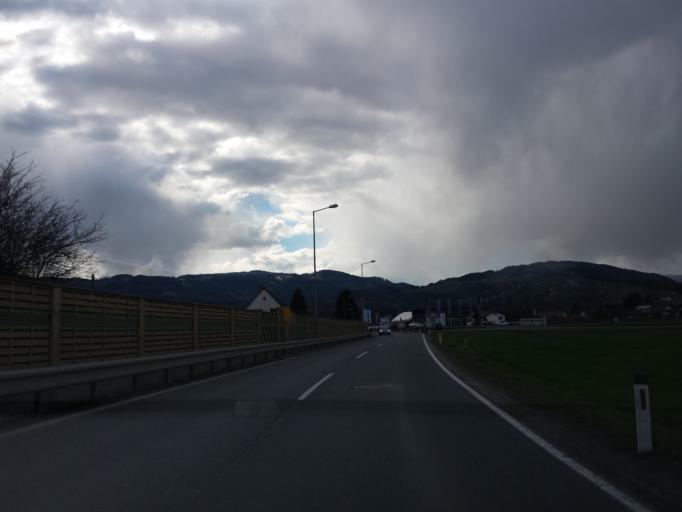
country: AT
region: Styria
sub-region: Politischer Bezirk Deutschlandsberg
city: Deutschlandsberg
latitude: 46.8159
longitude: 15.2385
